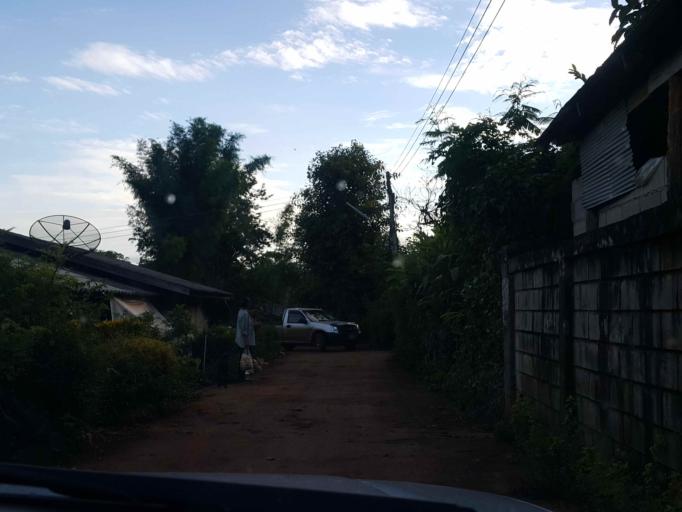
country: TH
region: Chiang Mai
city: Mae Chaem
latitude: 18.4963
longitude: 98.3965
